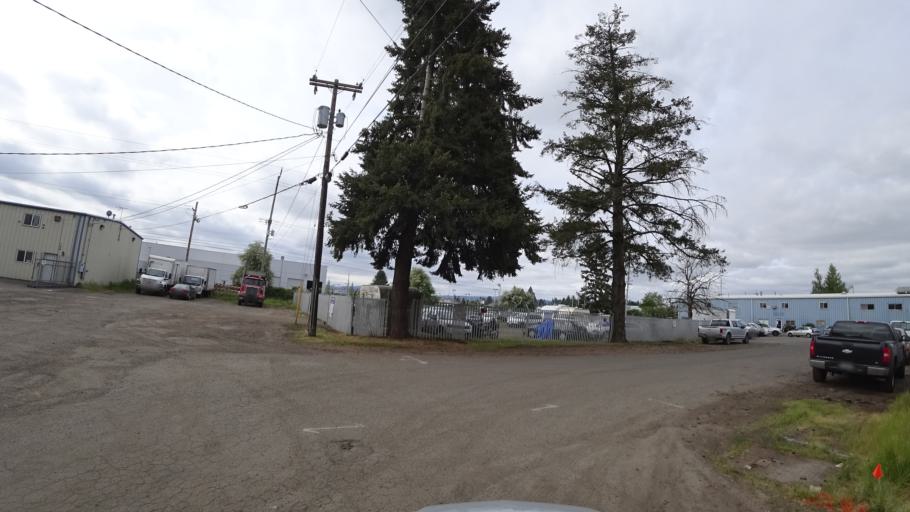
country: US
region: Oregon
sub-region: Washington County
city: Hillsboro
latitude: 45.5220
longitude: -122.9982
